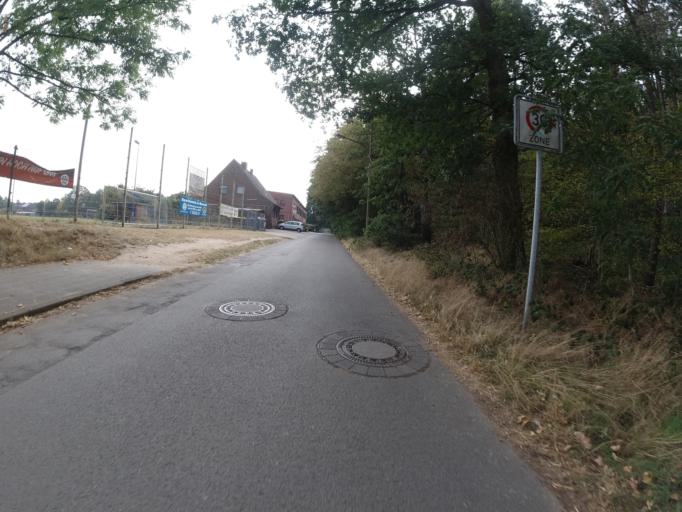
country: DE
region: North Rhine-Westphalia
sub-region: Regierungsbezirk Dusseldorf
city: Moers
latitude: 51.4082
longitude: 6.6489
